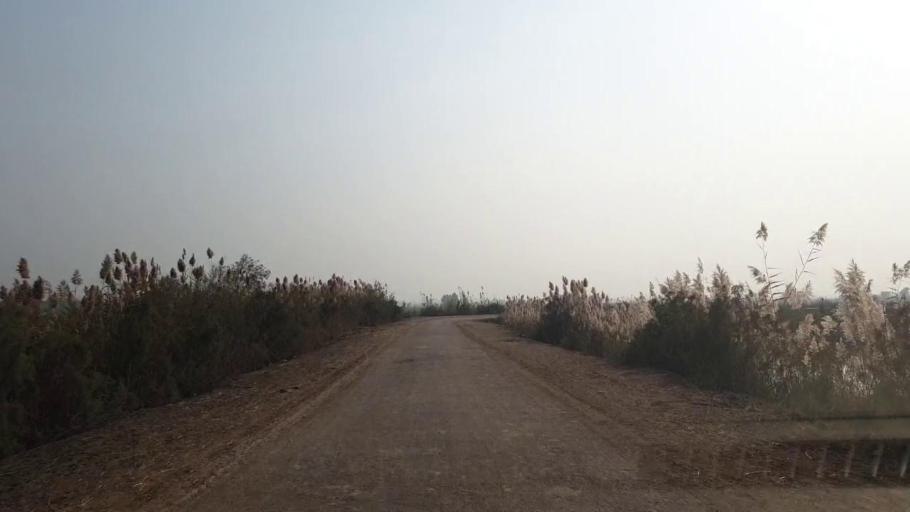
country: PK
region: Sindh
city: Shahdadpur
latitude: 25.9708
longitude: 68.5180
